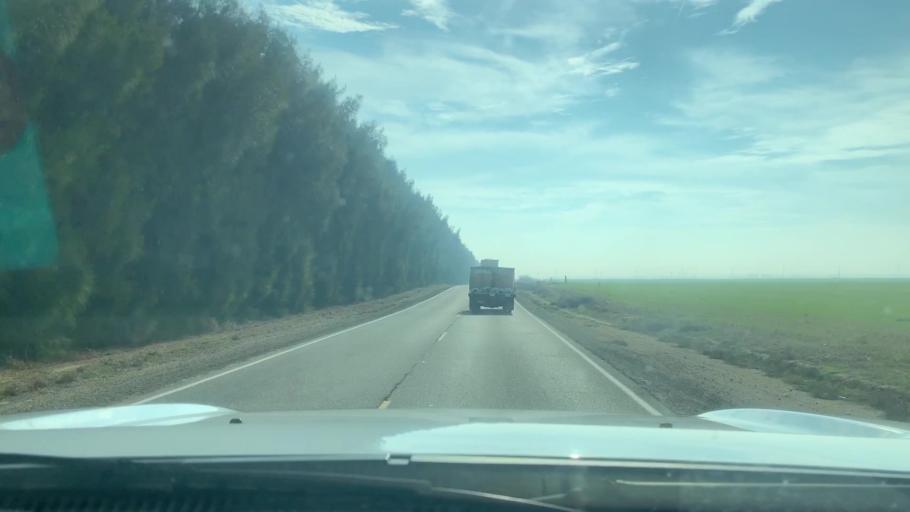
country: US
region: California
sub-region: Kern County
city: Lost Hills
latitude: 35.5106
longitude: -119.7481
